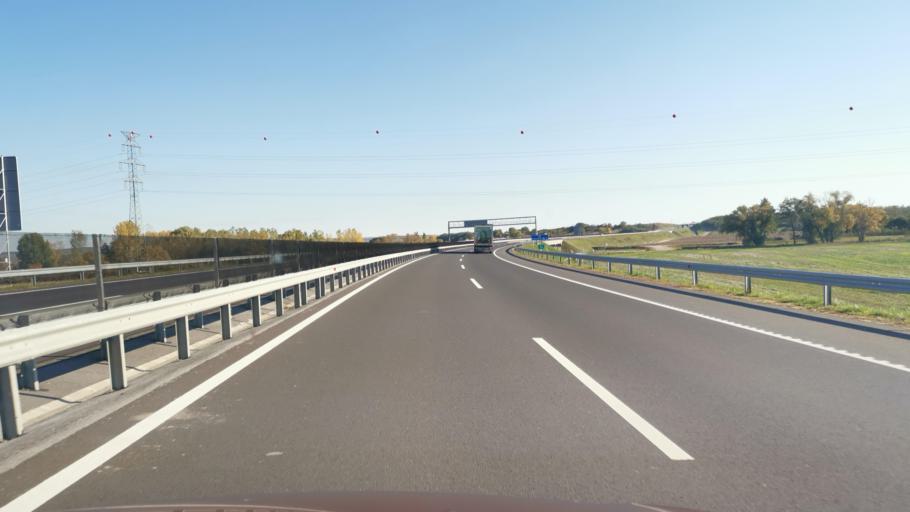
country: HU
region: Borsod-Abauj-Zemplen
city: Arnot
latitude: 48.1427
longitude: 20.8379
